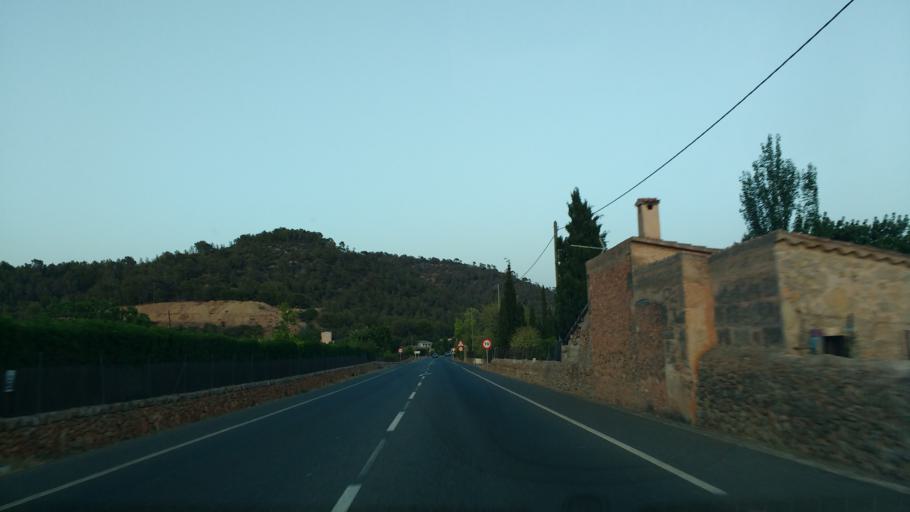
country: ES
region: Balearic Islands
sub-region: Illes Balears
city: Bunyola
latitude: 39.6671
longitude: 2.7093
